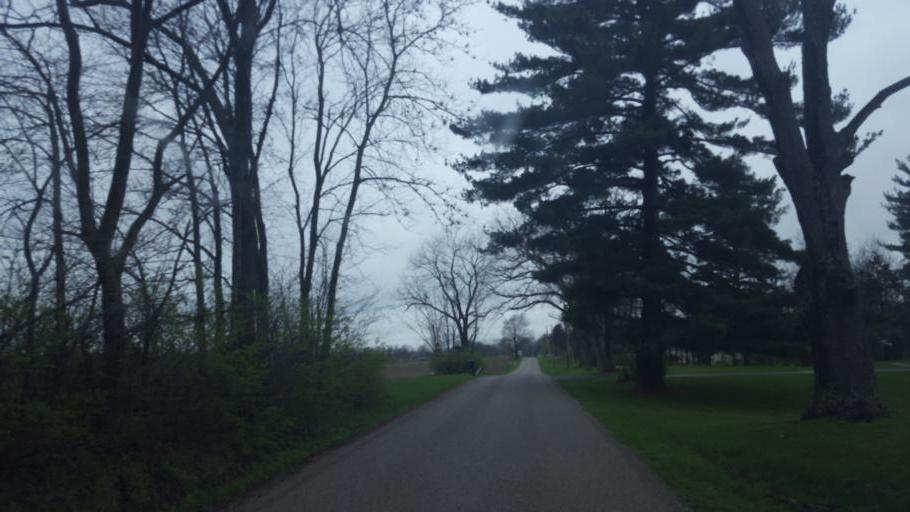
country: US
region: Ohio
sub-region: Morrow County
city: Mount Gilead
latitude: 40.5310
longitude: -82.8589
